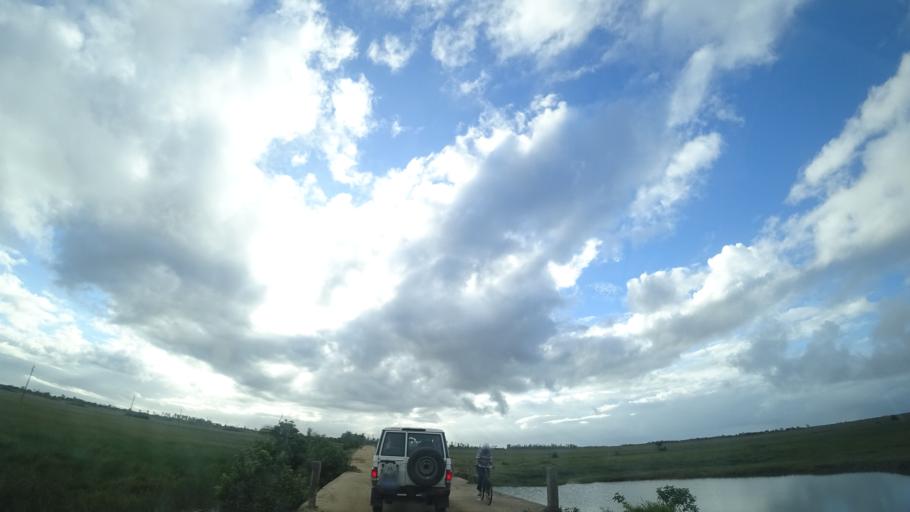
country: MZ
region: Sofala
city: Beira
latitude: -19.7282
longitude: 34.9860
